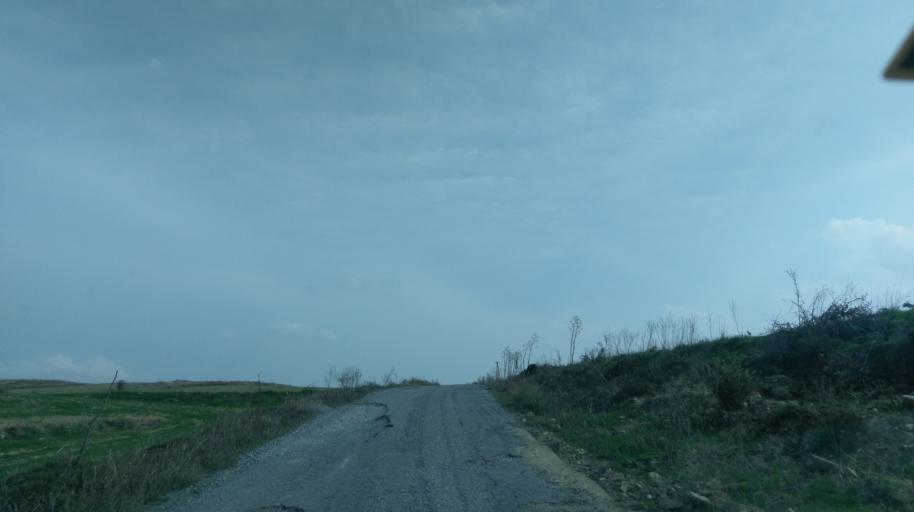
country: CY
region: Keryneia
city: Lapithos
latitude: 35.2642
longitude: 33.1130
